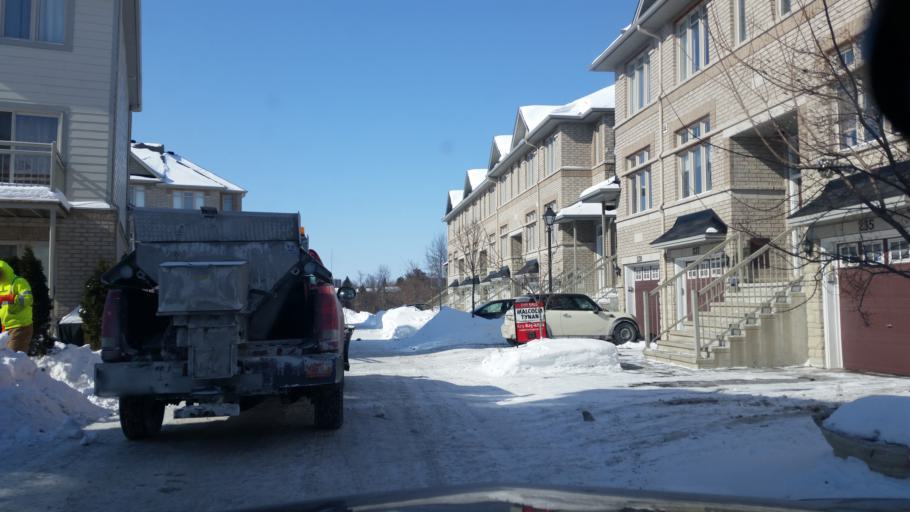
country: CA
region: Ontario
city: Ottawa
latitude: 45.3494
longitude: -75.7075
